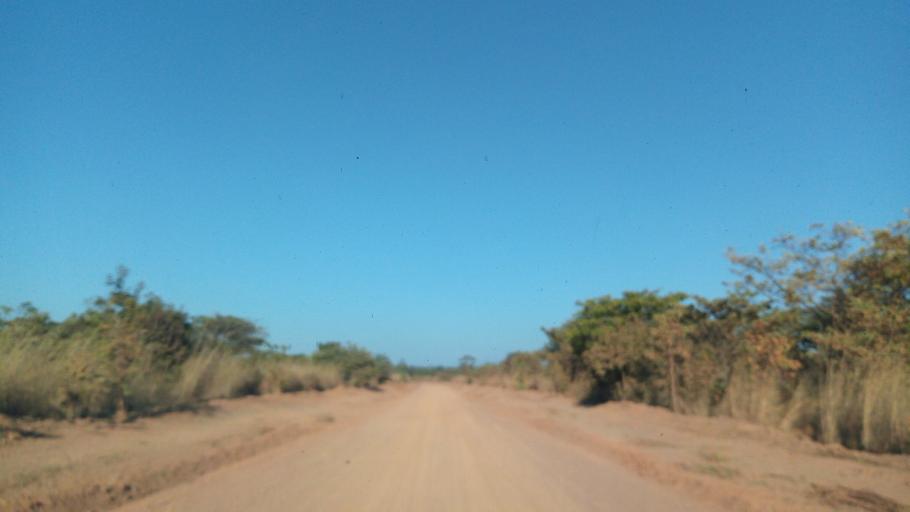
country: ZM
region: Luapula
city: Mwense
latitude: -10.4622
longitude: 28.5251
